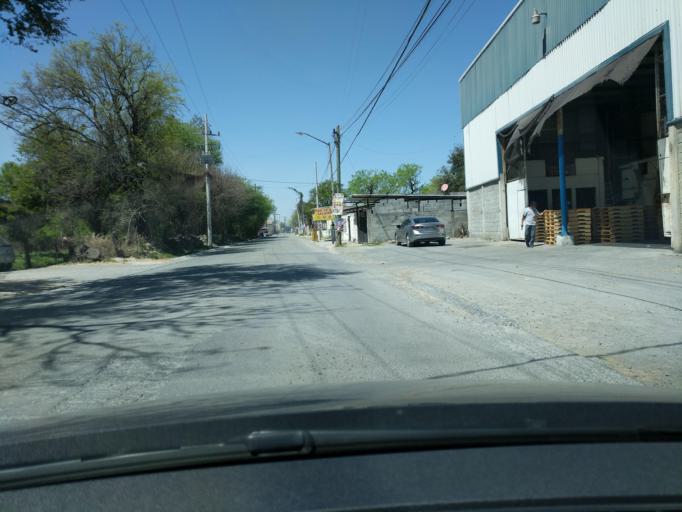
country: MX
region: Nuevo Leon
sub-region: Apodaca
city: Artemio Trevino
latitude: 25.8130
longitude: -100.1341
